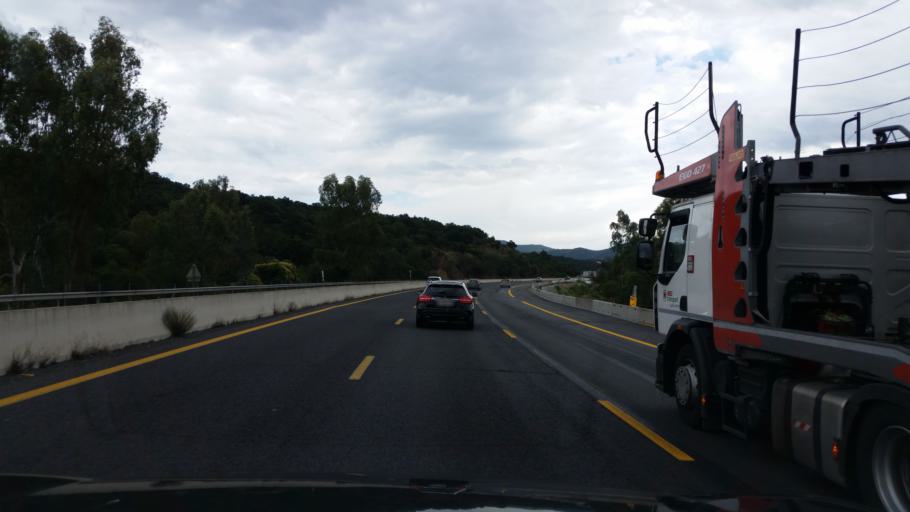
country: FR
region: Languedoc-Roussillon
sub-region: Departement des Pyrenees-Orientales
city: Maureillas-las-Illas
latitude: 42.4959
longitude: 2.8274
